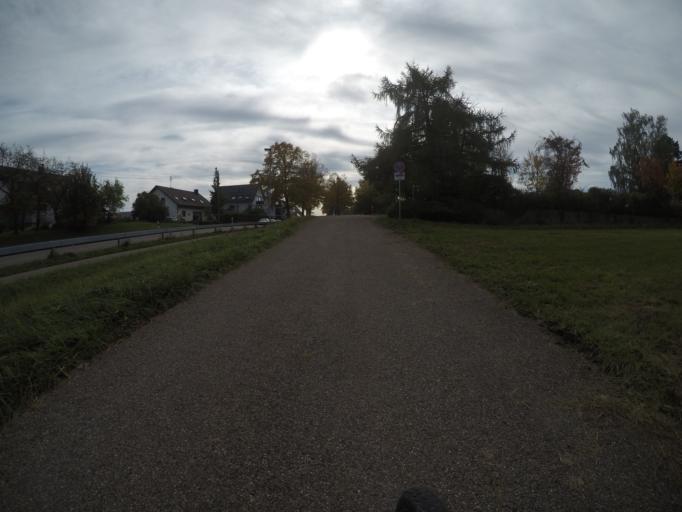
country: DE
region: Baden-Wuerttemberg
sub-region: Regierungsbezirk Stuttgart
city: Herrenberg
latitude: 48.6161
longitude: 8.8414
